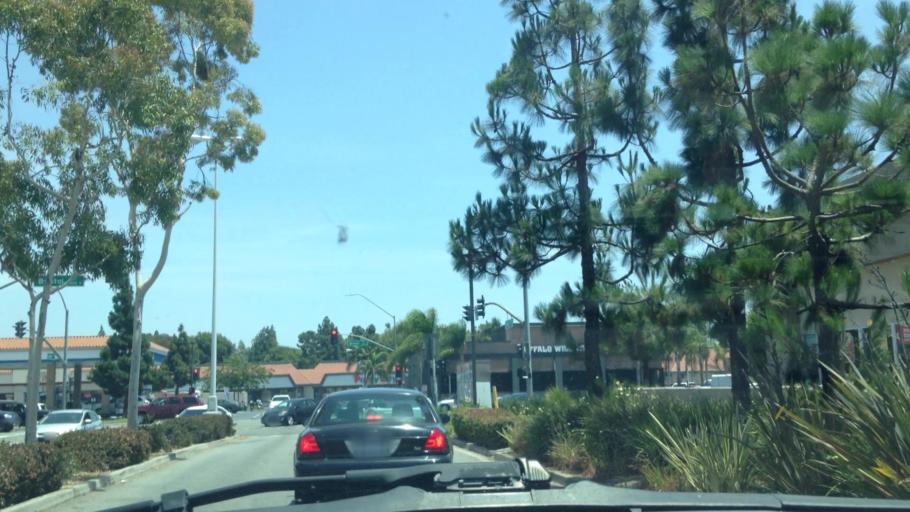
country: US
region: California
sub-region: Orange County
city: Santa Ana
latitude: 33.6969
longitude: -117.8863
